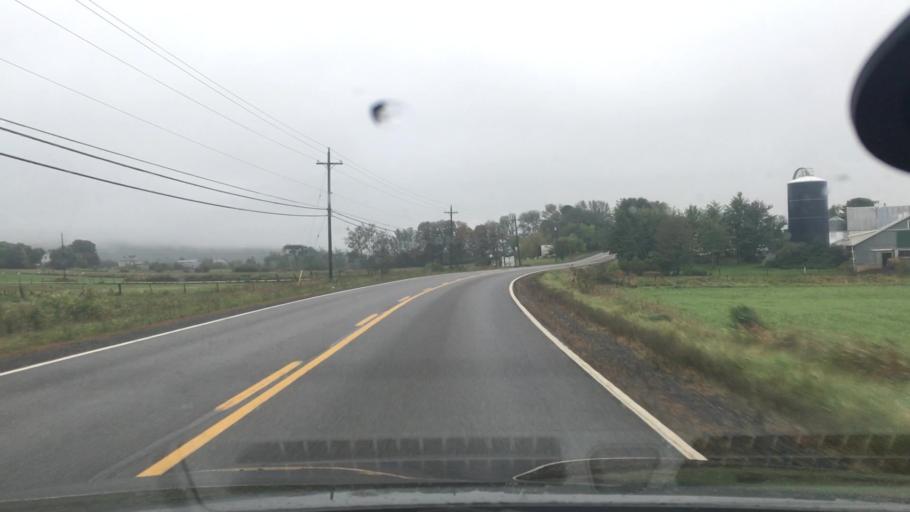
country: CA
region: Nova Scotia
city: Windsor
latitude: 44.9704
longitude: -64.1403
